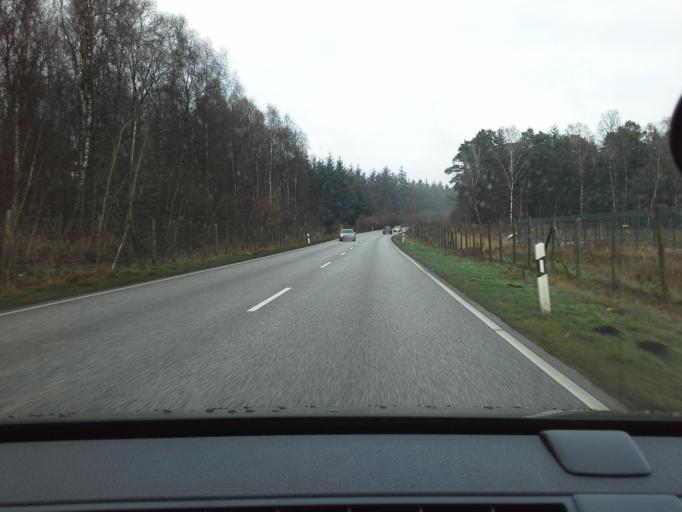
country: DE
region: Schleswig-Holstein
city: Henstedt-Ulzburg
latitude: 53.7435
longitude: 9.9831
